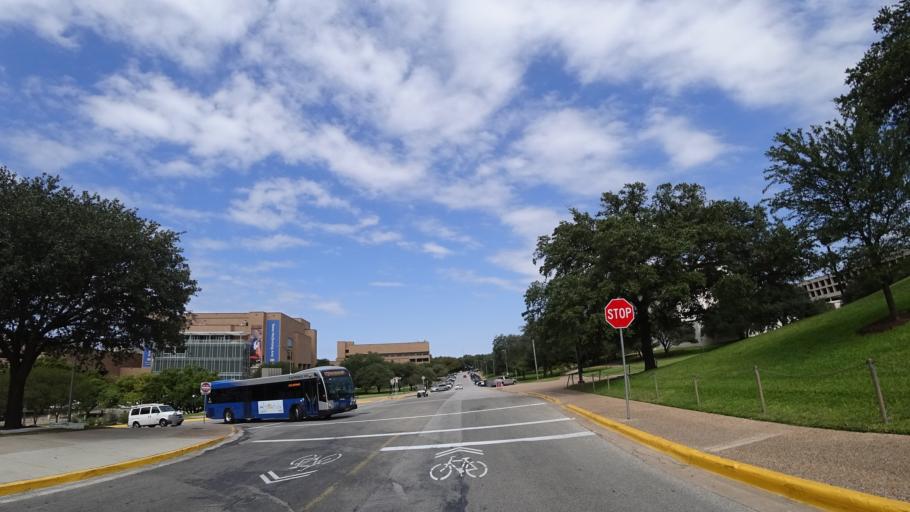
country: US
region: Texas
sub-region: Travis County
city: Austin
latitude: 30.2847
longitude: -97.7308
